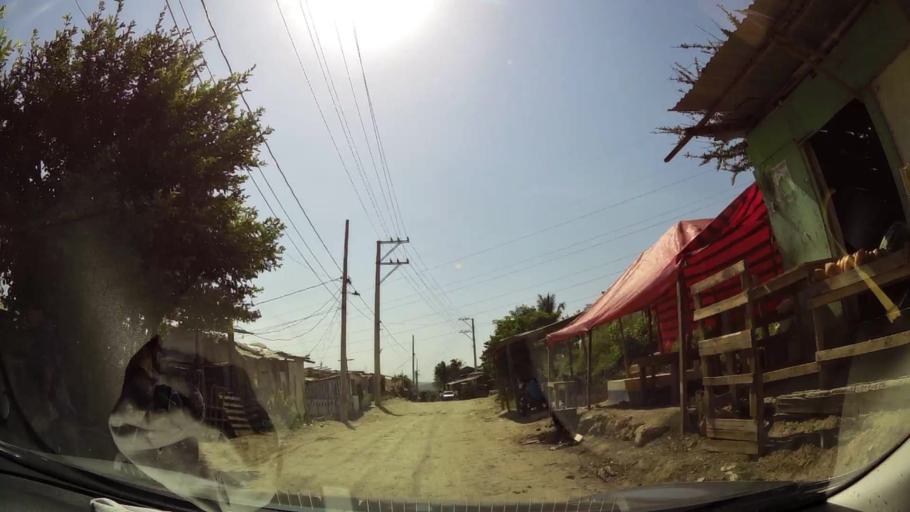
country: CO
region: Bolivar
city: Cartagena
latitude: 10.3626
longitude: -75.4891
